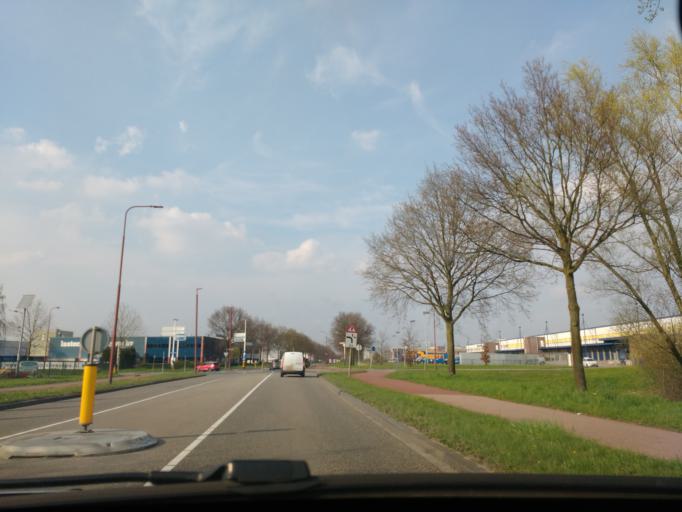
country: NL
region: Utrecht
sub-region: Gemeente Nieuwegein
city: Nieuwegein
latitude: 52.0268
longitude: 5.1042
